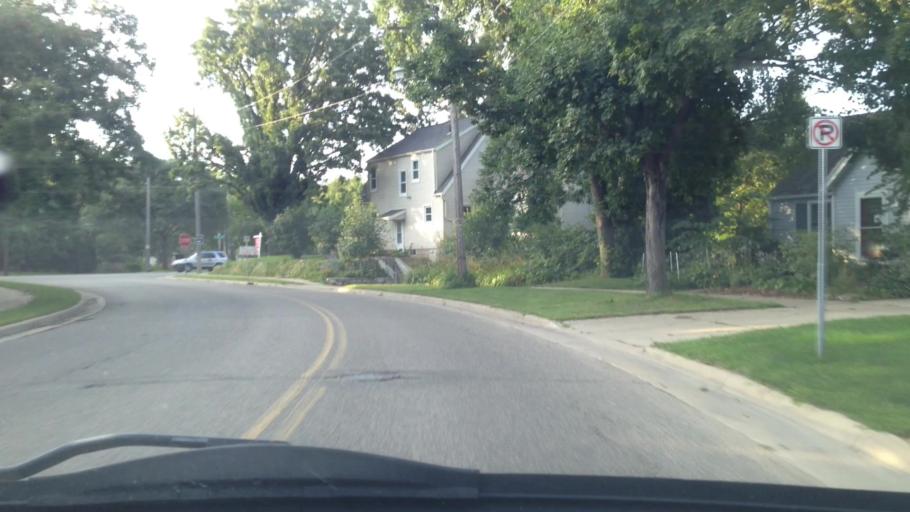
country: US
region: Minnesota
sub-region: Olmsted County
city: Rochester
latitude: 44.0101
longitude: -92.4725
